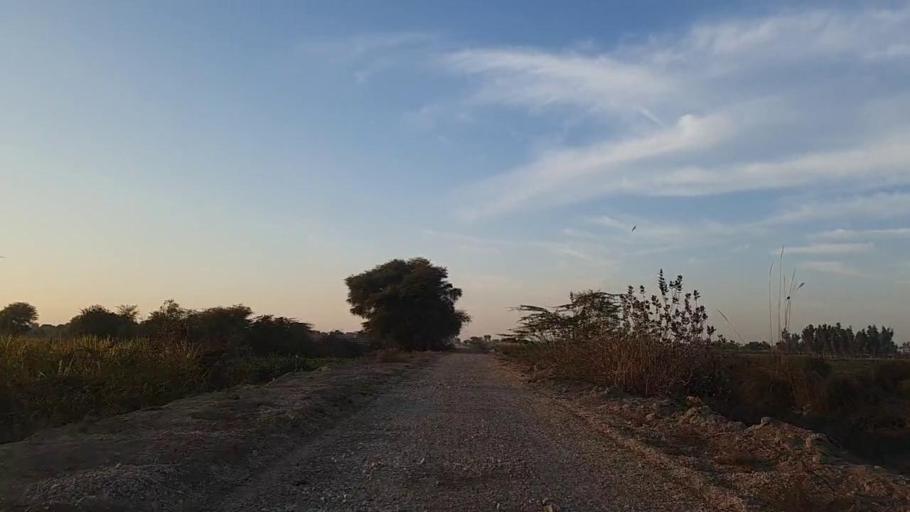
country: PK
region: Sindh
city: Bandhi
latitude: 26.6165
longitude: 68.3537
